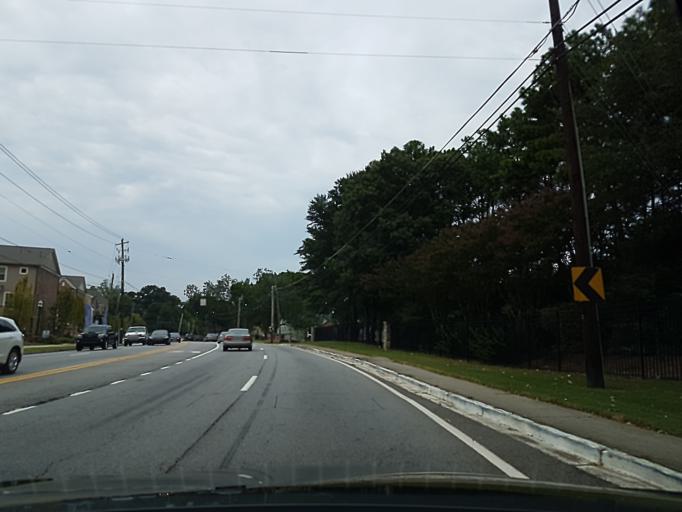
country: US
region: Georgia
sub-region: DeKalb County
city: North Druid Hills
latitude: 33.8219
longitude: -84.3155
